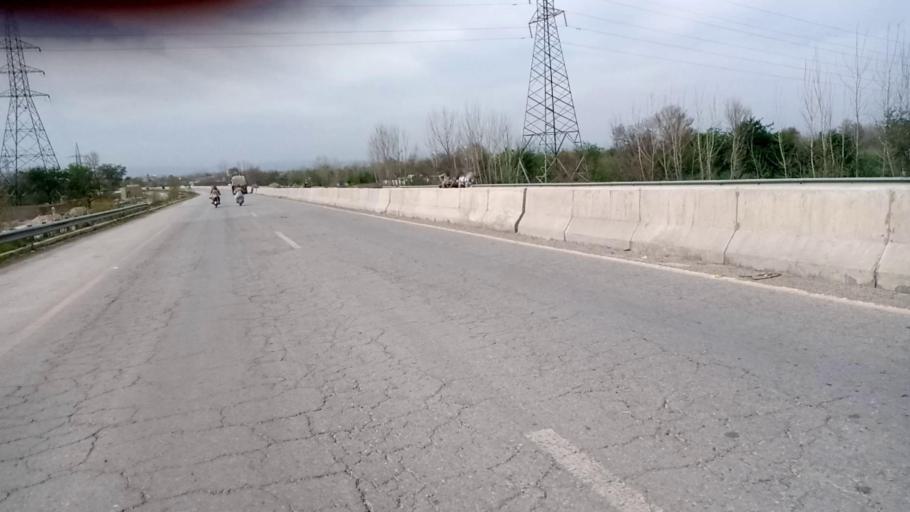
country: PK
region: Khyber Pakhtunkhwa
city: Peshawar
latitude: 34.0635
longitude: 71.6029
